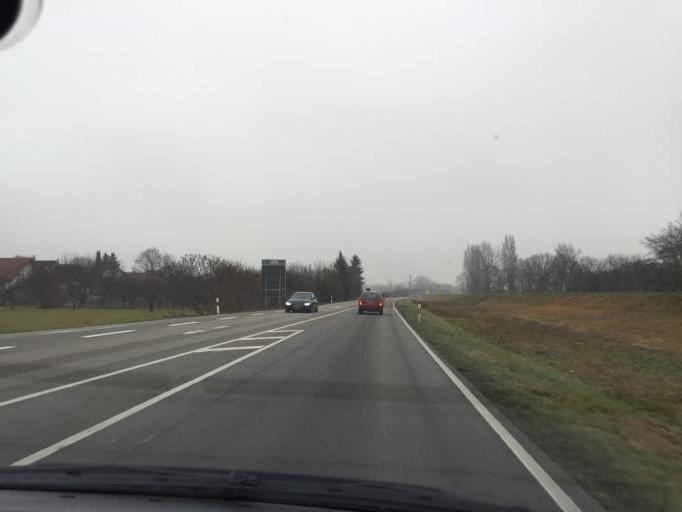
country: DE
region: Baden-Wuerttemberg
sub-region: Freiburg Region
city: Breisach am Rhein
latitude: 48.0187
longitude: 7.6052
